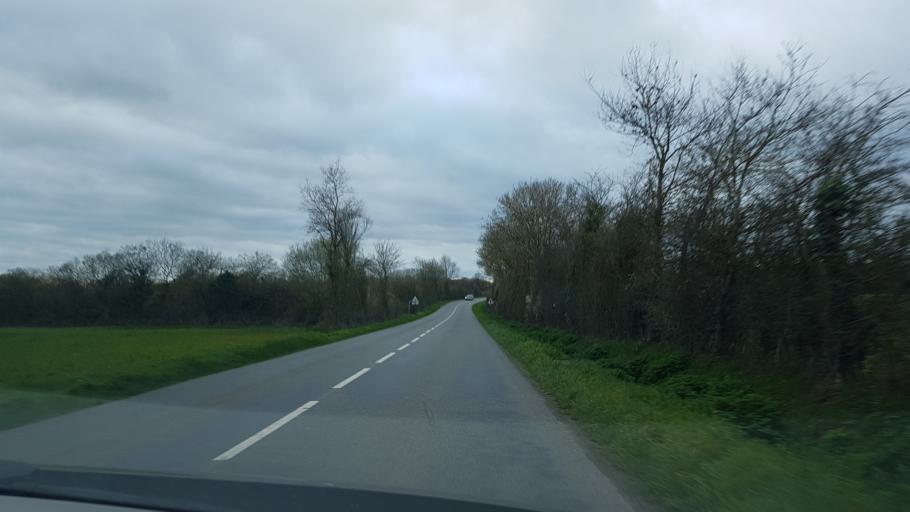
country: FR
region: Pays de la Loire
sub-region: Departement de la Loire-Atlantique
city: La Grigonnais
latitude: 47.5176
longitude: -1.6603
